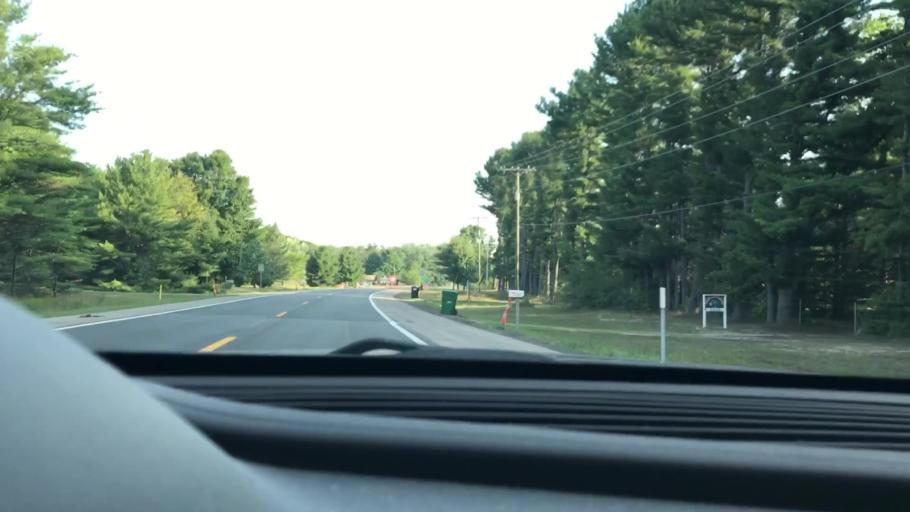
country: US
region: Michigan
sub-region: Antrim County
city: Bellaire
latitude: 45.0693
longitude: -85.3588
